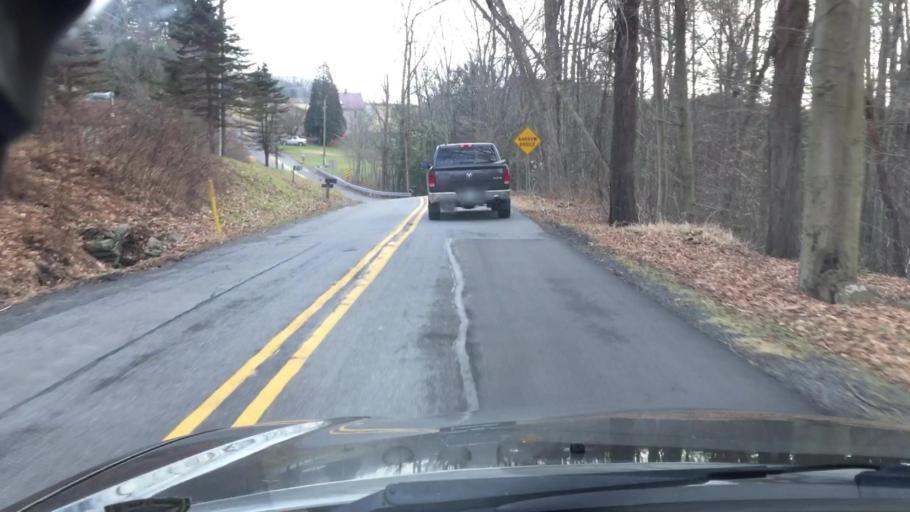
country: US
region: Pennsylvania
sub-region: Luzerne County
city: Back Mountain
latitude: 41.3247
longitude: -76.0676
